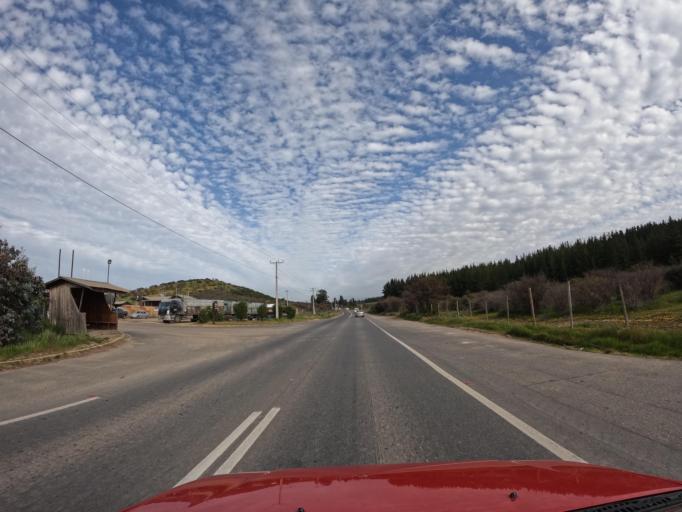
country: CL
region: O'Higgins
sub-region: Provincia de Colchagua
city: Santa Cruz
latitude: -34.3212
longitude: -71.7601
